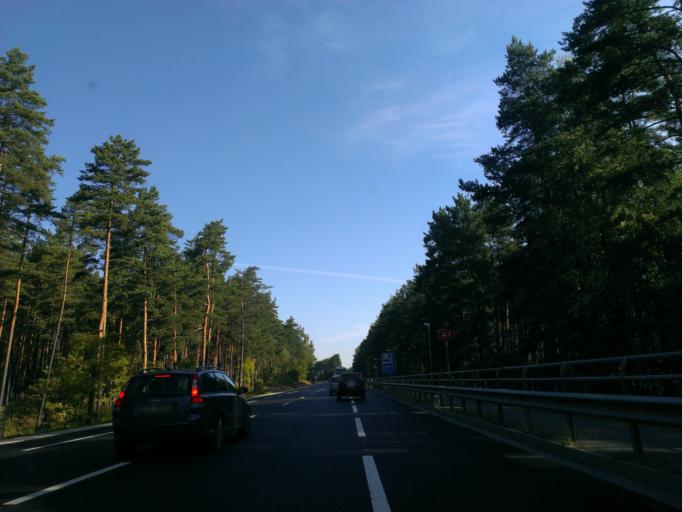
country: LV
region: Adazi
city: Adazi
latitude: 57.0555
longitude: 24.3207
